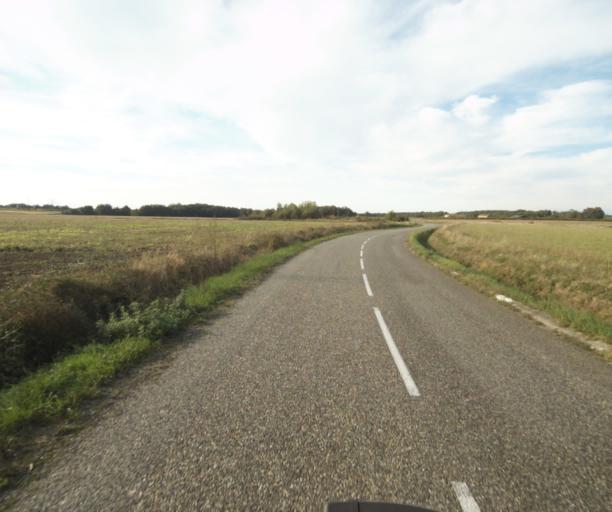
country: FR
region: Midi-Pyrenees
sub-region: Departement du Tarn-et-Garonne
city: Finhan
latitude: 43.9090
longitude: 1.1150
